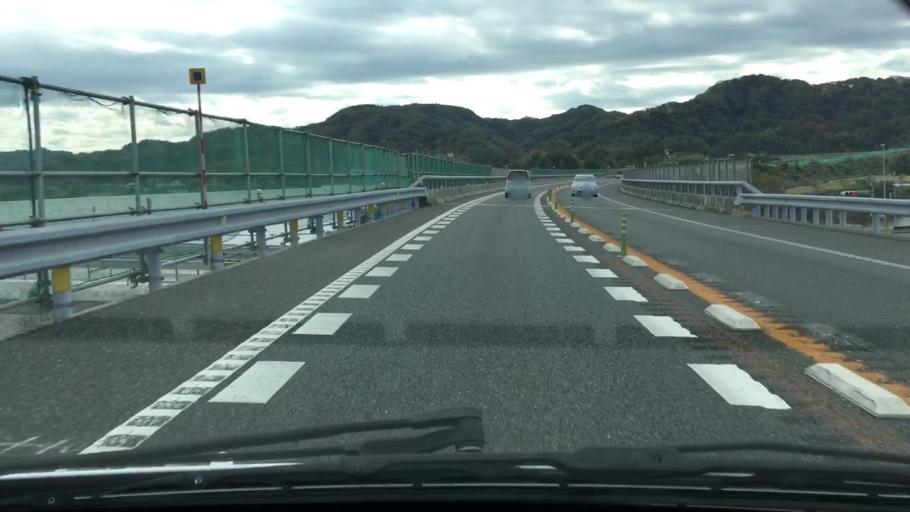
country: JP
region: Chiba
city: Kimitsu
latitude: 35.2193
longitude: 139.8854
